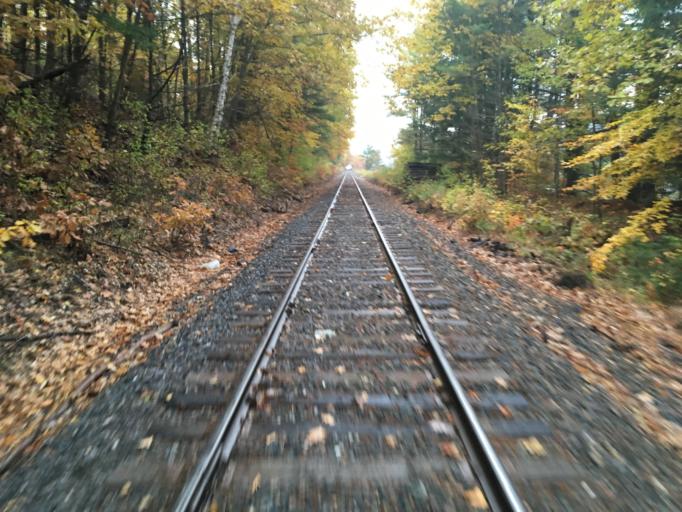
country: US
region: New Hampshire
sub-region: Grafton County
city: Hanover
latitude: 43.7355
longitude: -72.2624
